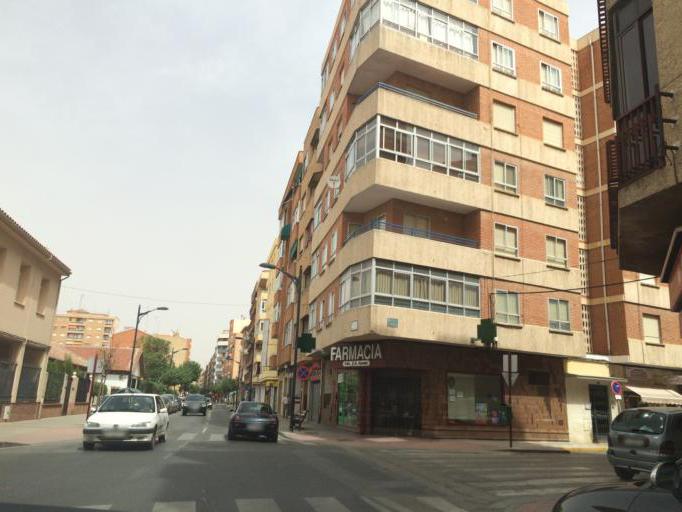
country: ES
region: Castille-La Mancha
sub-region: Provincia de Albacete
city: Albacete
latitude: 38.9854
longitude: -1.8629
